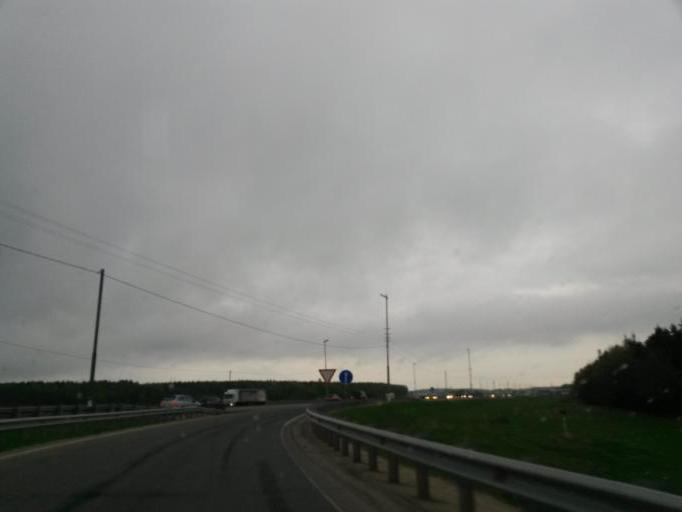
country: RU
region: Moskovskaya
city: L'vovskiy
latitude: 55.3340
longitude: 37.5707
